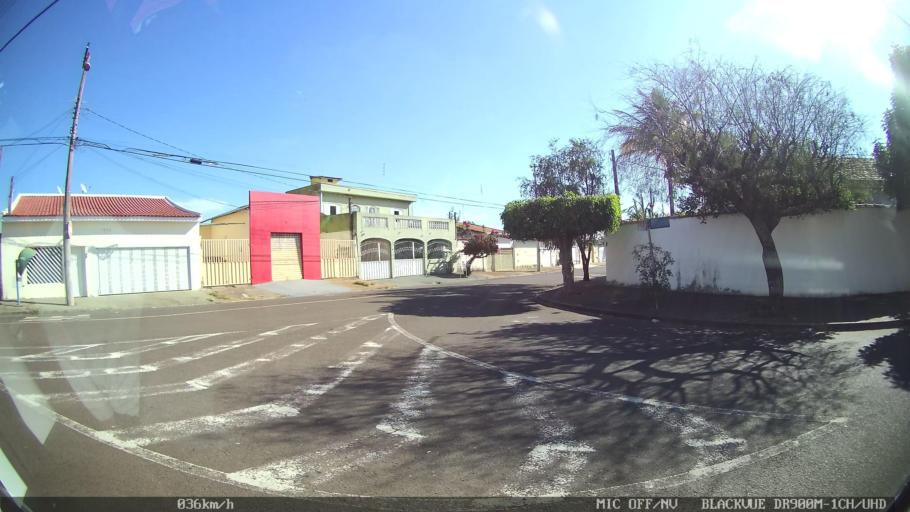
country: BR
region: Sao Paulo
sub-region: Franca
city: Franca
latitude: -20.4886
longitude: -47.4153
